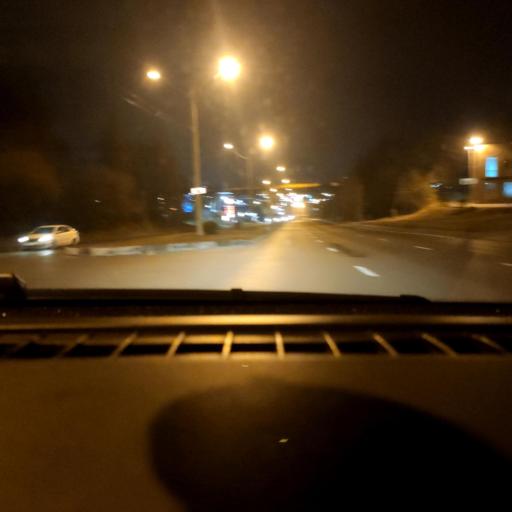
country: RU
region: Voronezj
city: Pridonskoy
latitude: 51.6732
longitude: 39.1182
